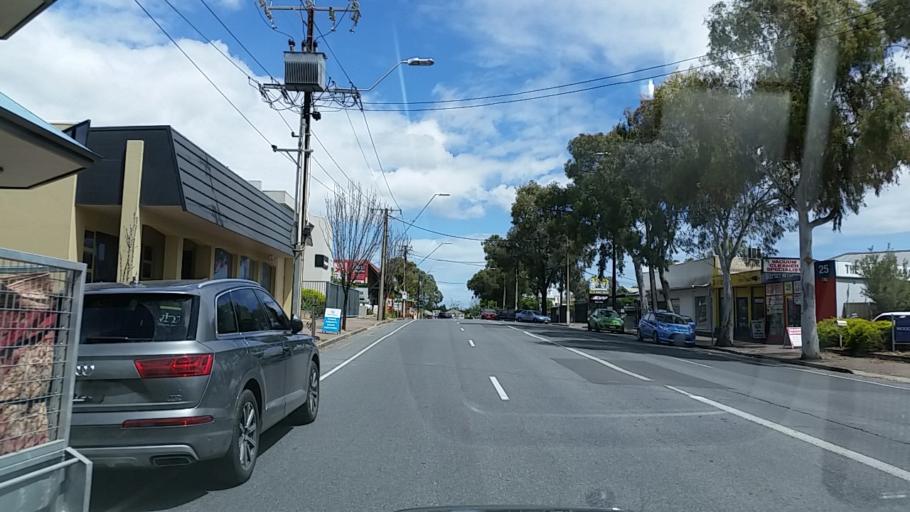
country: AU
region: South Australia
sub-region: Norwood Payneham St Peters
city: Trinity Gardens
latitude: -34.9156
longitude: 138.6255
